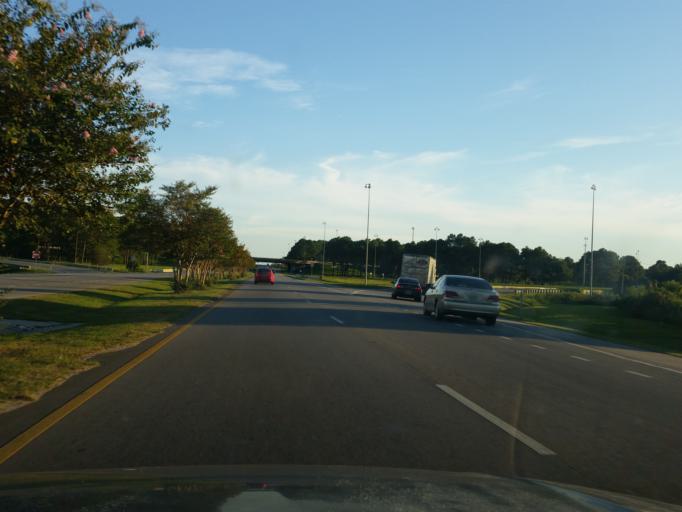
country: US
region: Alabama
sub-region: Mobile County
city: Tillmans Corner
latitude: 30.5850
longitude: -88.1700
